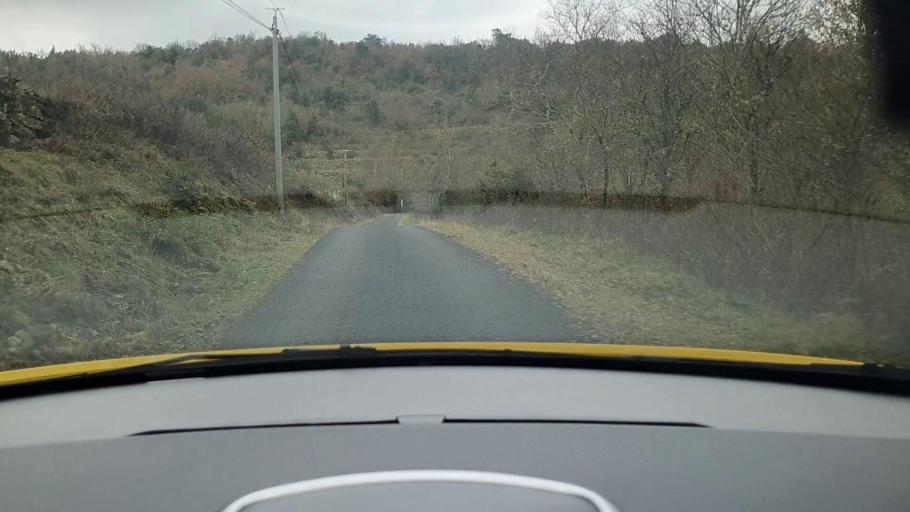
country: FR
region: Languedoc-Roussillon
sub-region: Departement du Gard
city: Saint-Florent-sur-Auzonnet
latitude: 44.2671
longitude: 4.1226
